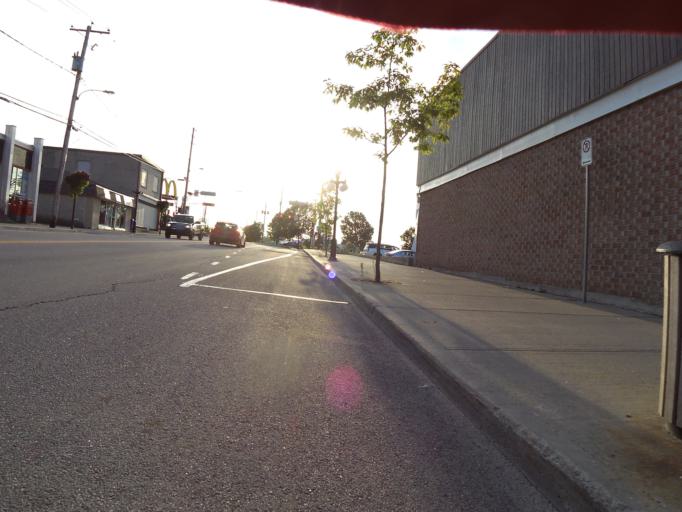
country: CA
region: Quebec
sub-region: Outaouais
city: Maniwaki
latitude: 46.3751
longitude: -75.9806
